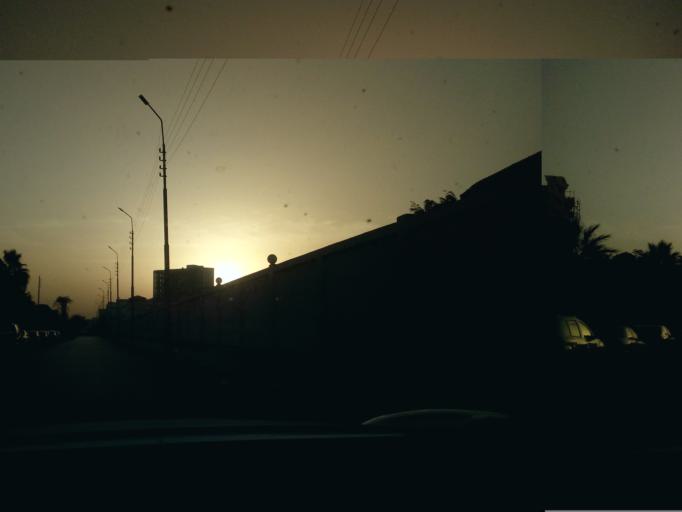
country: EG
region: Muhafazat al Qahirah
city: Cairo
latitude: 30.0926
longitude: 31.3447
